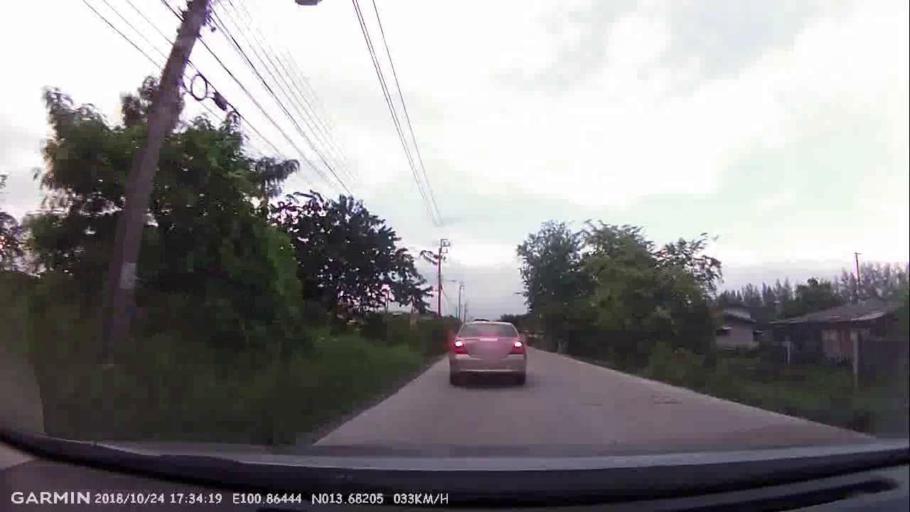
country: TH
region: Samut Prakan
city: Ban Khlong Bang Sao Thong
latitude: 13.6821
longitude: 100.8644
